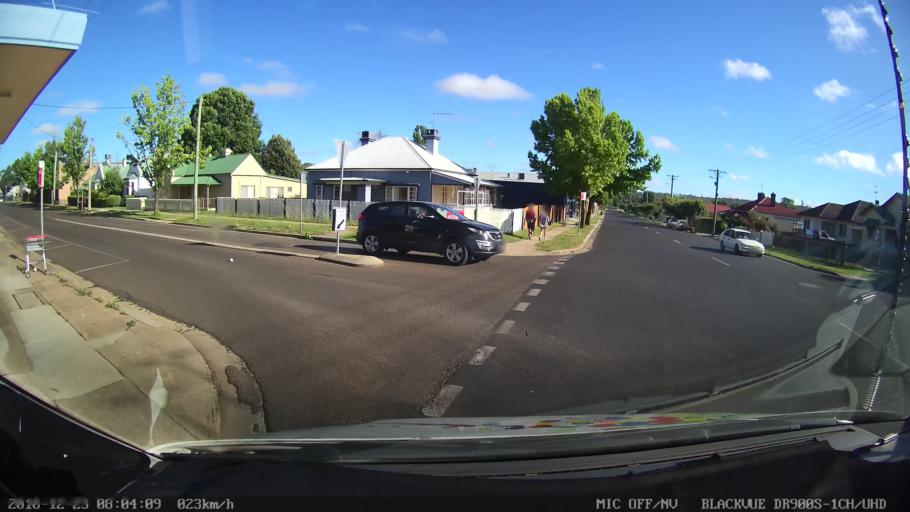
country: AU
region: New South Wales
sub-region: Armidale Dumaresq
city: Armidale
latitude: -30.5164
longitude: 151.6713
